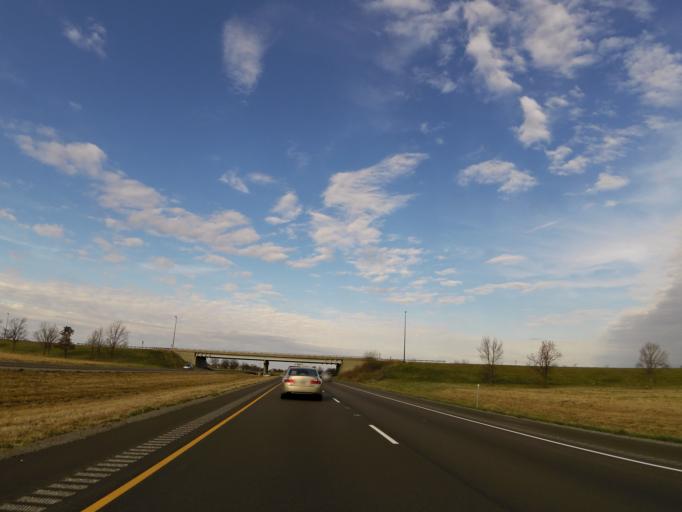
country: US
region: Illinois
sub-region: Washington County
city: Okawville
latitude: 38.4388
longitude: -89.5282
